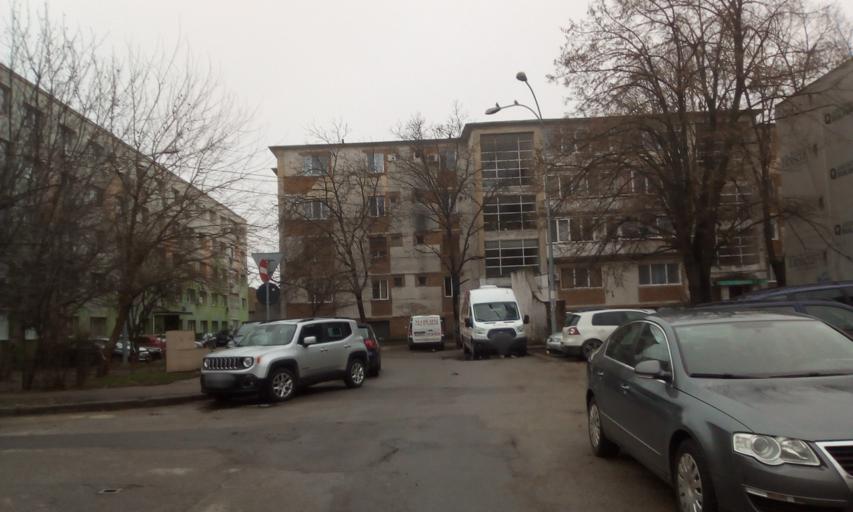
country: RO
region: Timis
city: Timisoara
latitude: 45.7502
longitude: 21.2444
